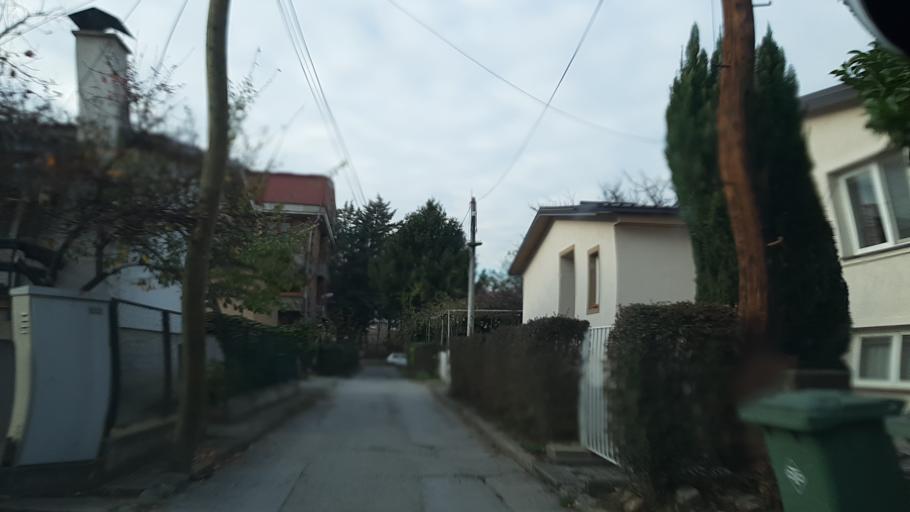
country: MK
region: Kisela Voda
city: Usje
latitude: 41.9778
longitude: 21.4523
